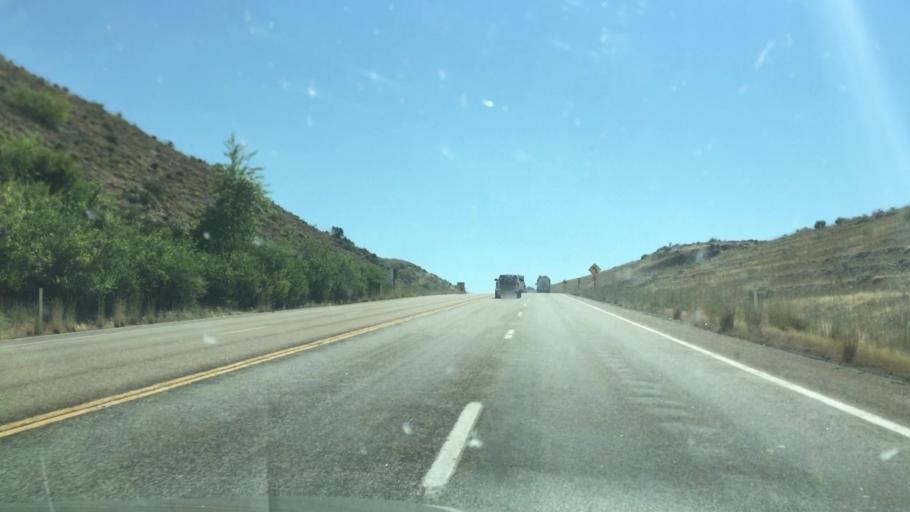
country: US
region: Idaho
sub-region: Ada County
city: Eagle
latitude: 43.8390
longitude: -116.2405
